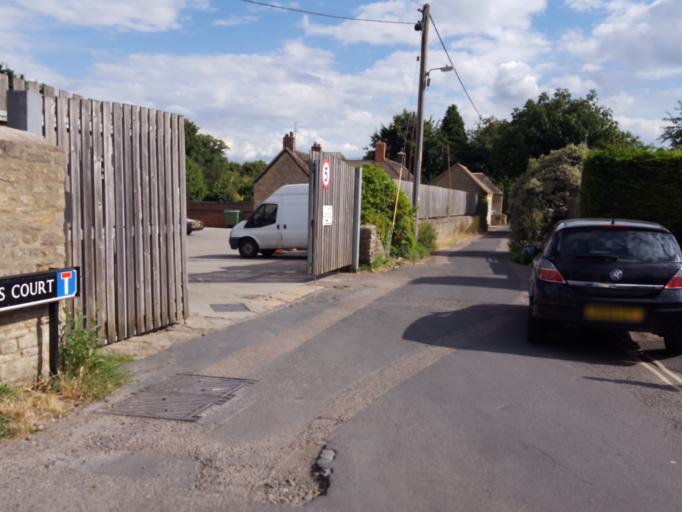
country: GB
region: England
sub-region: Oxfordshire
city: Witney
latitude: 51.7833
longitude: -1.4885
